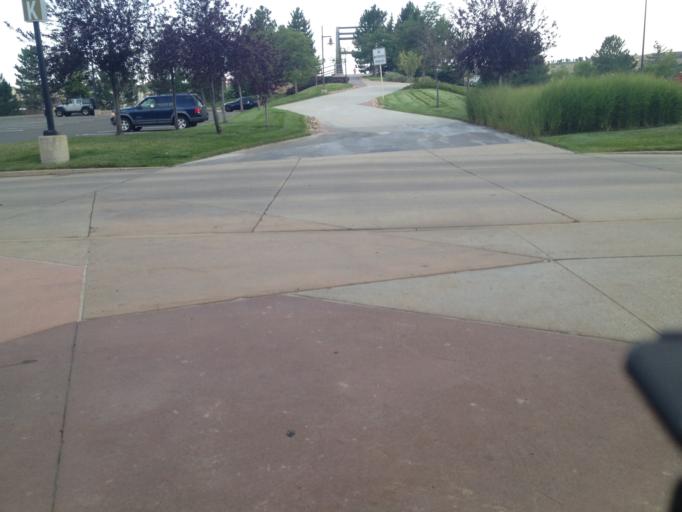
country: US
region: Colorado
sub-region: Boulder County
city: Superior
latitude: 39.9299
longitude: -105.1355
